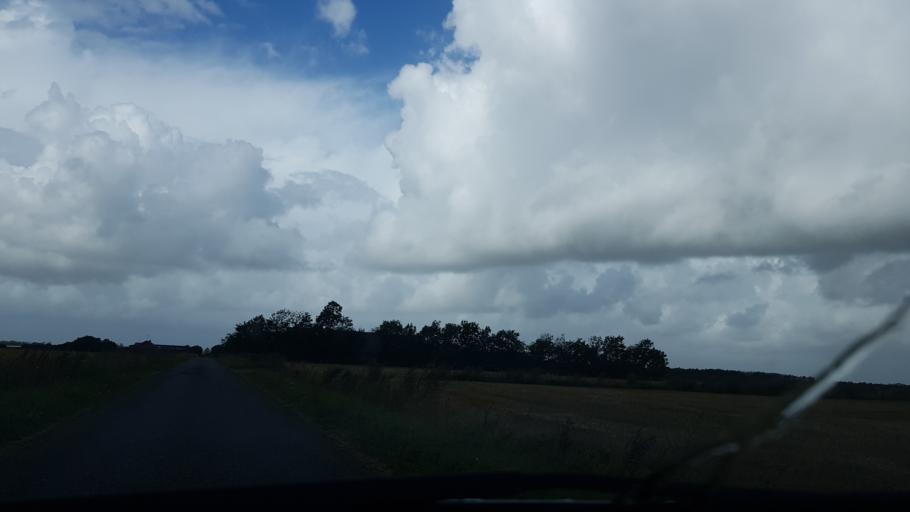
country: DK
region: South Denmark
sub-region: Tonder Kommune
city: Sherrebek
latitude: 55.2427
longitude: 8.7936
